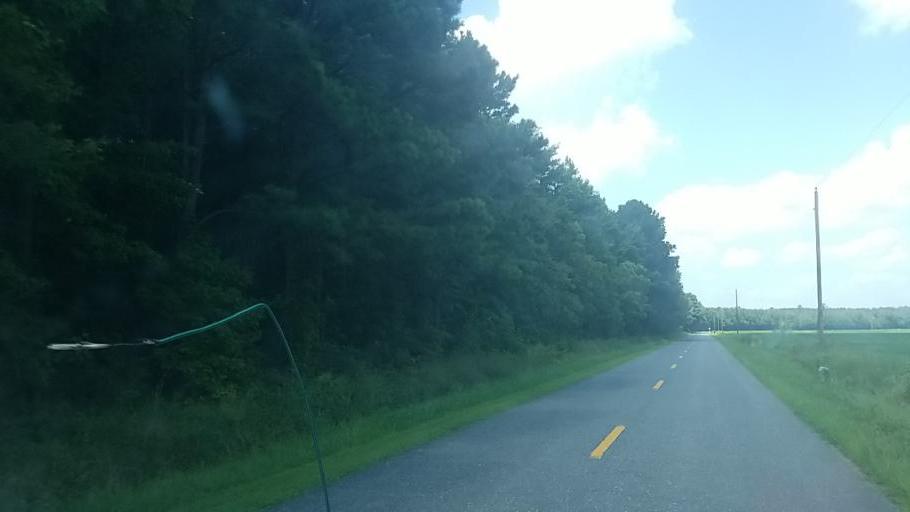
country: US
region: Maryland
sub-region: Dorchester County
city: Hurlock
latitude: 38.4651
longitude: -75.8459
